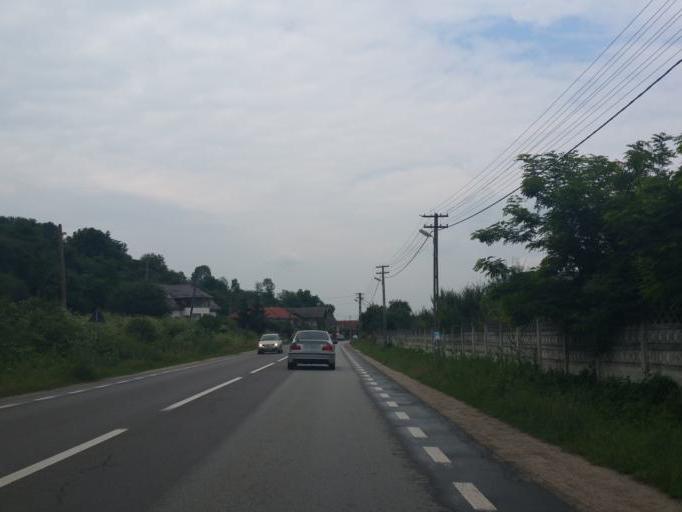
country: RO
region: Salaj
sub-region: Comuna Zimbor
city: Zimbor
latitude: 47.0018
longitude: 23.2558
